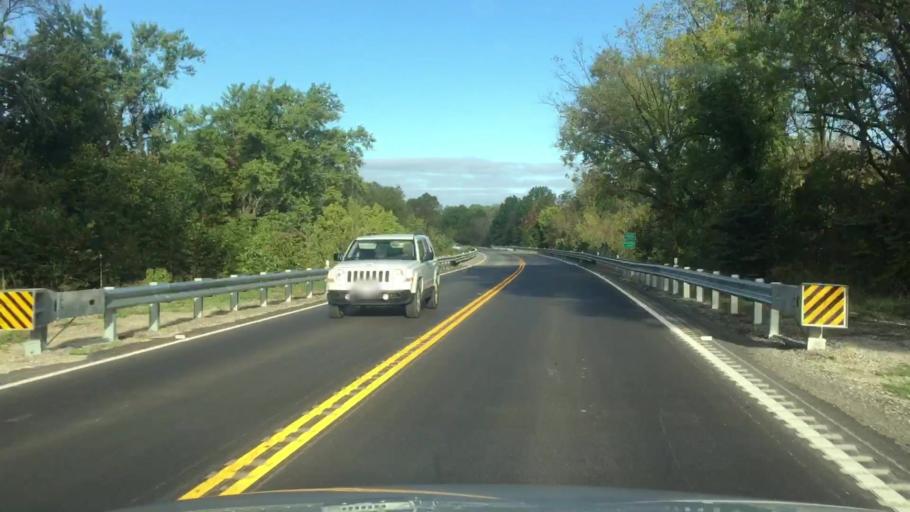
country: US
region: Missouri
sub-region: Howard County
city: New Franklin
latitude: 38.9924
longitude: -92.5638
